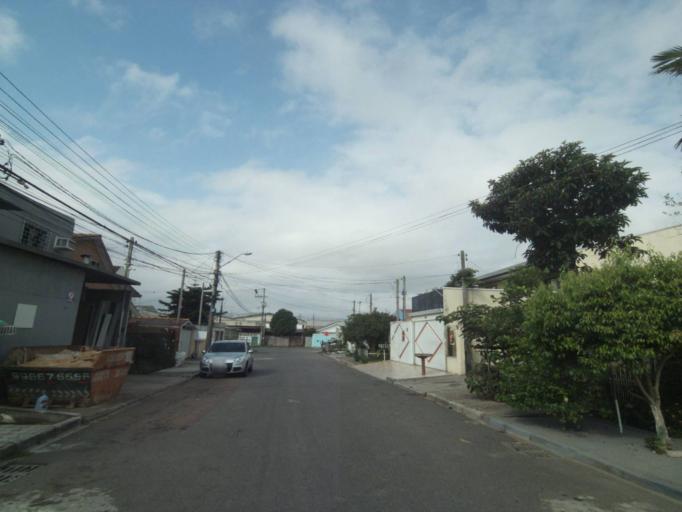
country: BR
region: Parana
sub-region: Sao Jose Dos Pinhais
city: Sao Jose dos Pinhais
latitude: -25.5369
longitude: -49.2579
